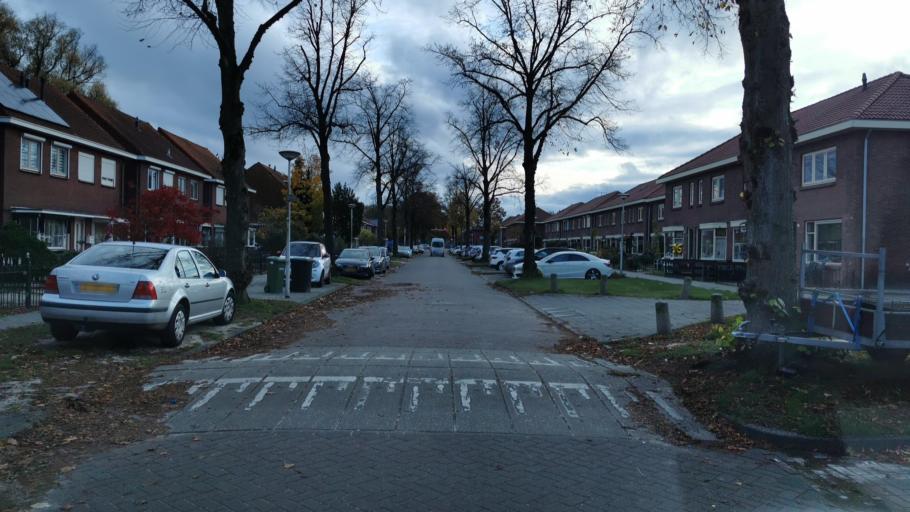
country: NL
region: Overijssel
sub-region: Gemeente Enschede
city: Enschede
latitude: 52.2191
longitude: 6.9459
